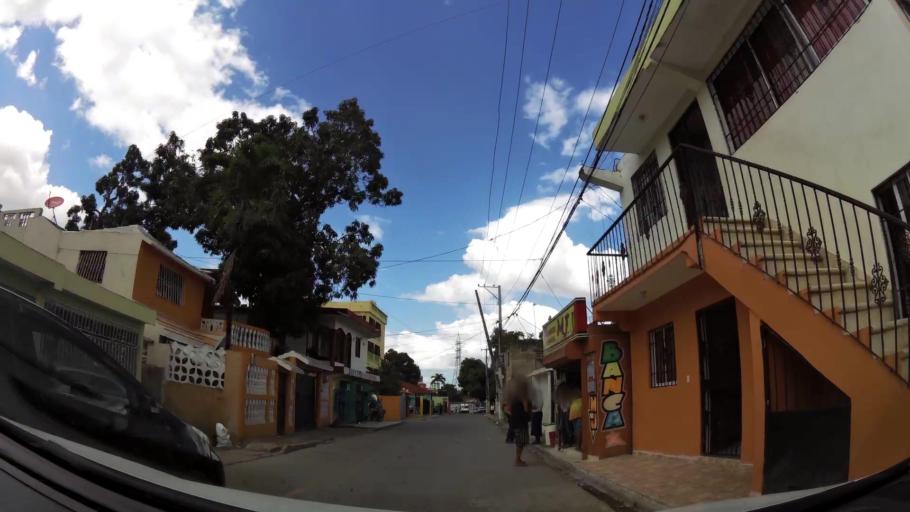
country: DO
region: Nacional
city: Ensanche Luperon
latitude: 18.5325
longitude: -69.9077
